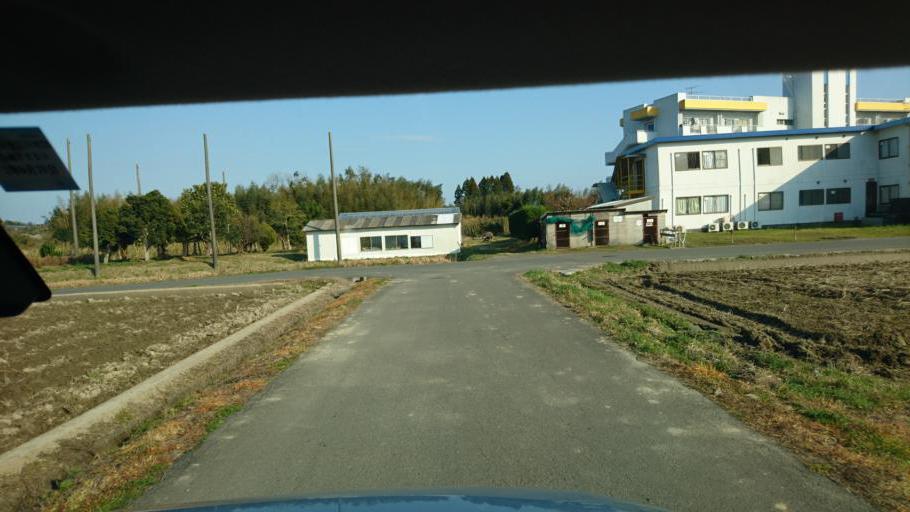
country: JP
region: Miyazaki
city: Miyazaki-shi
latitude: 32.0064
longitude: 131.4394
